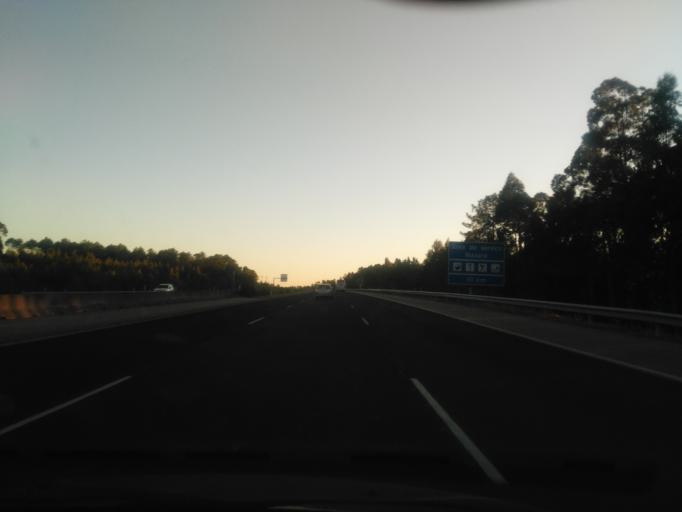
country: PT
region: Leiria
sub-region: Leiria
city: Maceira
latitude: 39.6959
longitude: -8.9269
